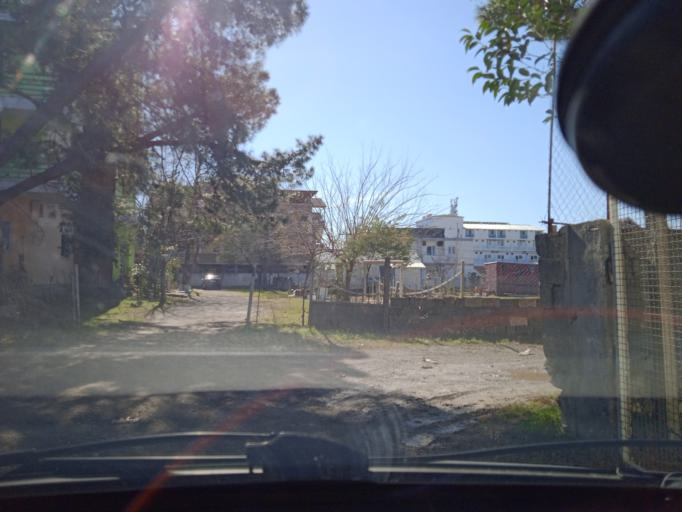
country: AL
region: Shkoder
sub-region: Rrethi i Shkodres
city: Velipoje
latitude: 41.8641
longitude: 19.4211
